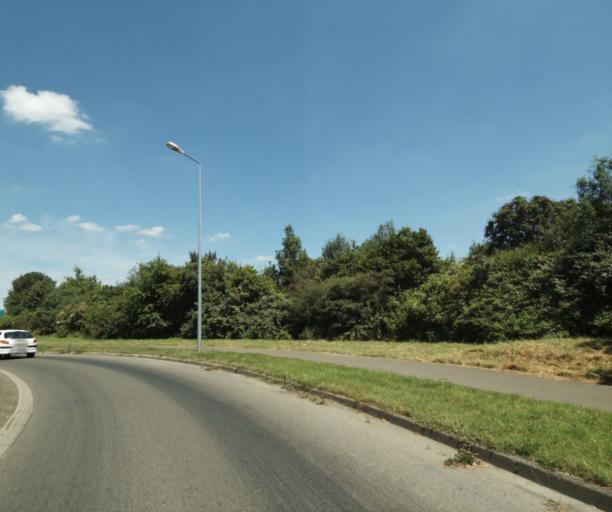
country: FR
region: Pays de la Loire
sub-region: Departement de la Mayenne
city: Change
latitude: 48.0775
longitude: -0.7953
